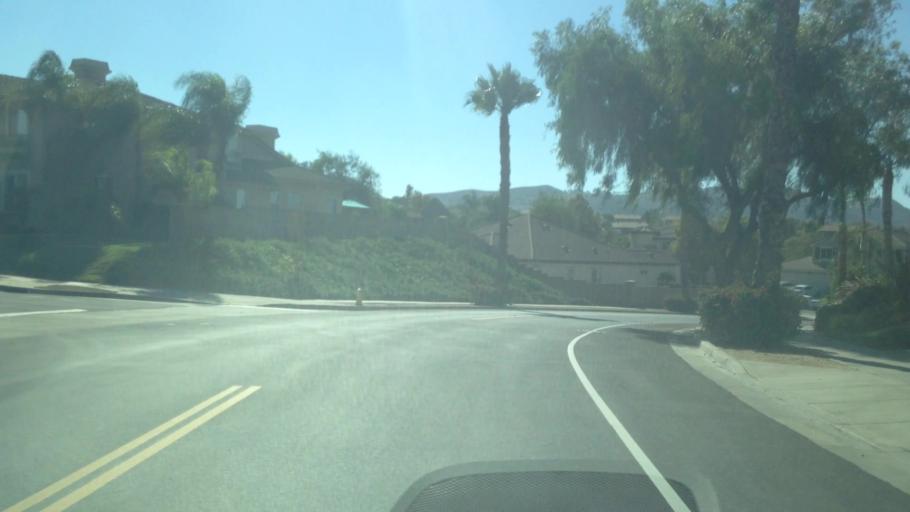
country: US
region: California
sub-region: Riverside County
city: Home Gardens
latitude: 33.8691
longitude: -117.4419
